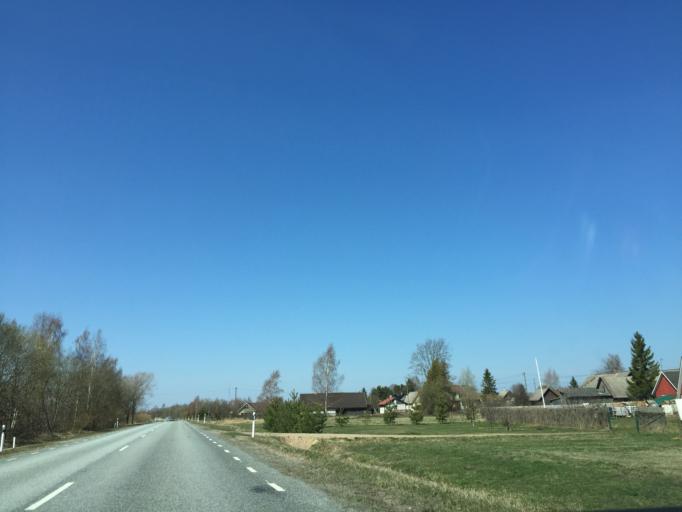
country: EE
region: Jogevamaa
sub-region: Mustvee linn
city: Mustvee
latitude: 58.7823
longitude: 26.9740
